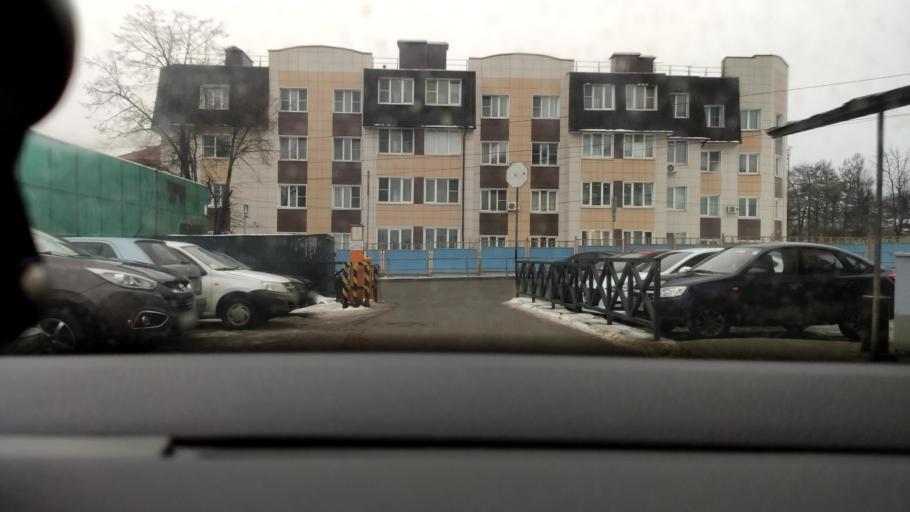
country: RU
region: Moskovskaya
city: Sergiyev Posad
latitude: 56.3012
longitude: 38.1341
